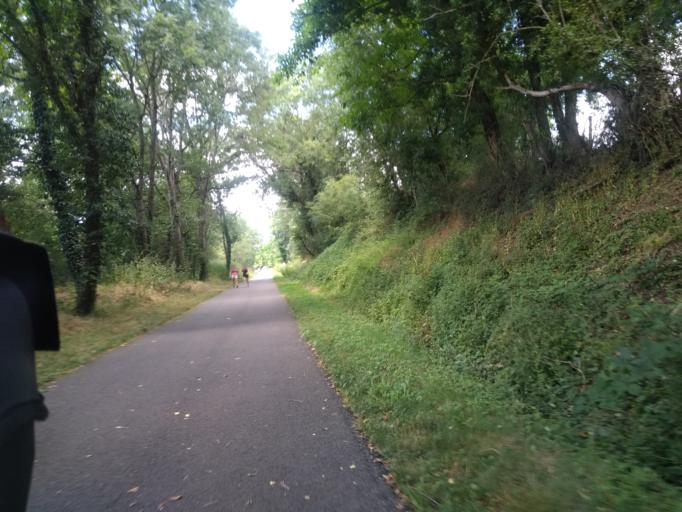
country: FR
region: Rhone-Alpes
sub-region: Departement de la Loire
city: Briennon
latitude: 46.1977
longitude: 4.0822
